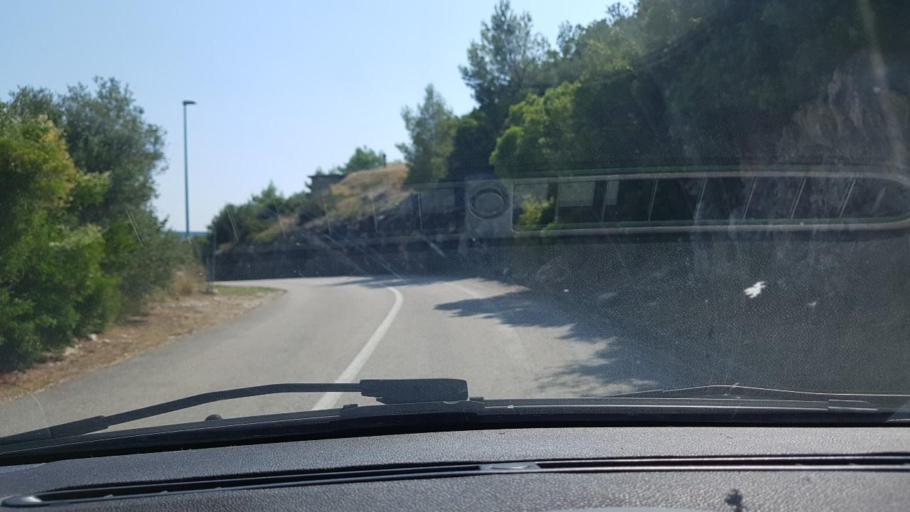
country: HR
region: Dubrovacko-Neretvanska
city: Podgora
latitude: 42.7815
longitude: 17.8689
